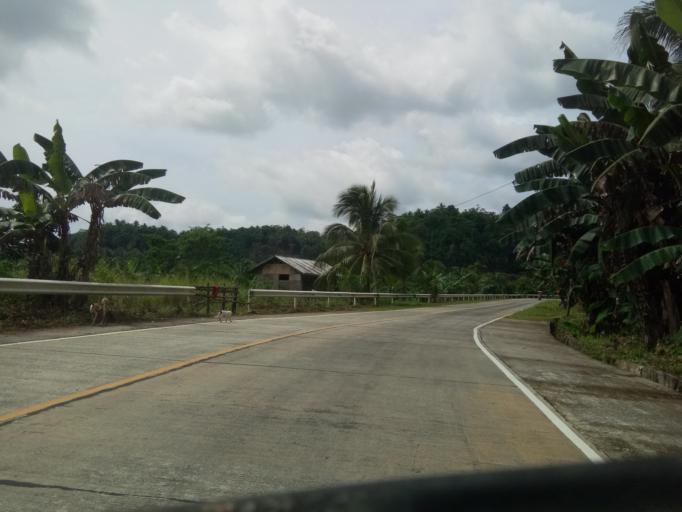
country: PH
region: Caraga
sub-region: Province of Surigao del Norte
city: Pilar
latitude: 9.8918
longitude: 126.0762
